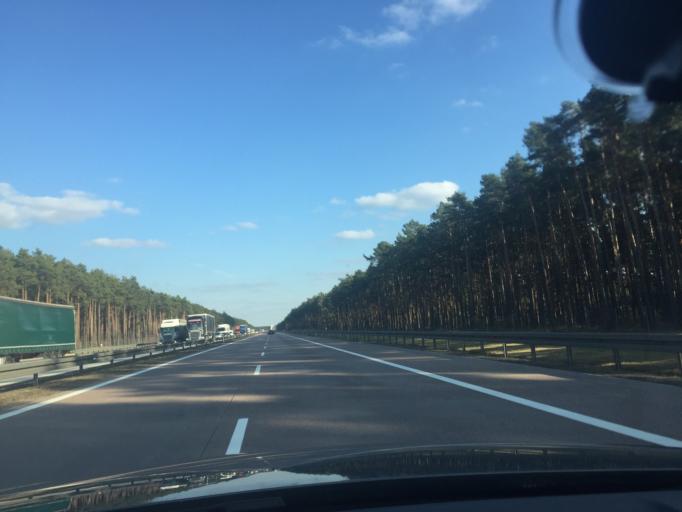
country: PL
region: Lubusz
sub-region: Powiat slubicki
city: Rzepin
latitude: 52.3352
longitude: 14.7654
